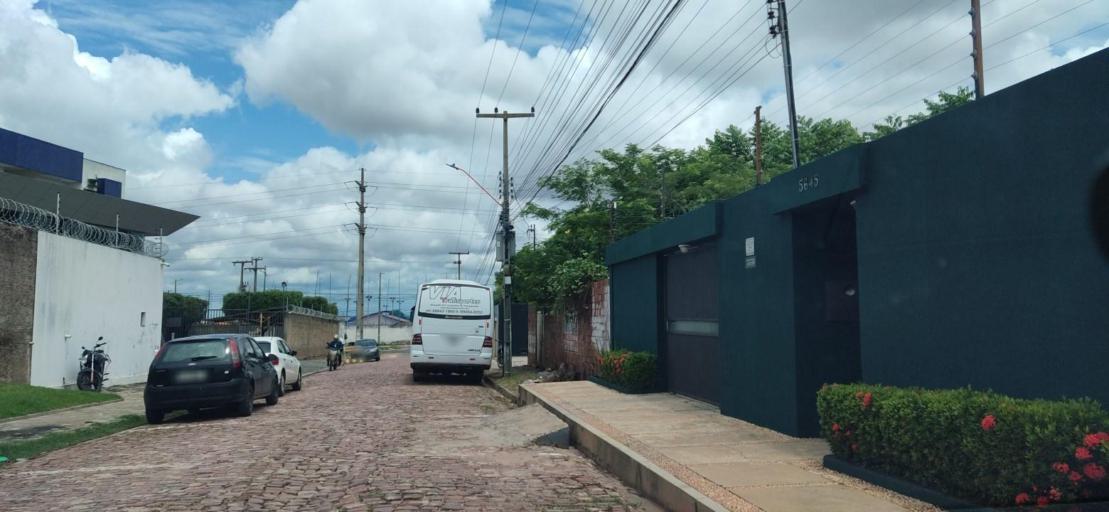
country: BR
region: Piaui
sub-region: Teresina
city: Teresina
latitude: -5.0724
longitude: -42.7507
